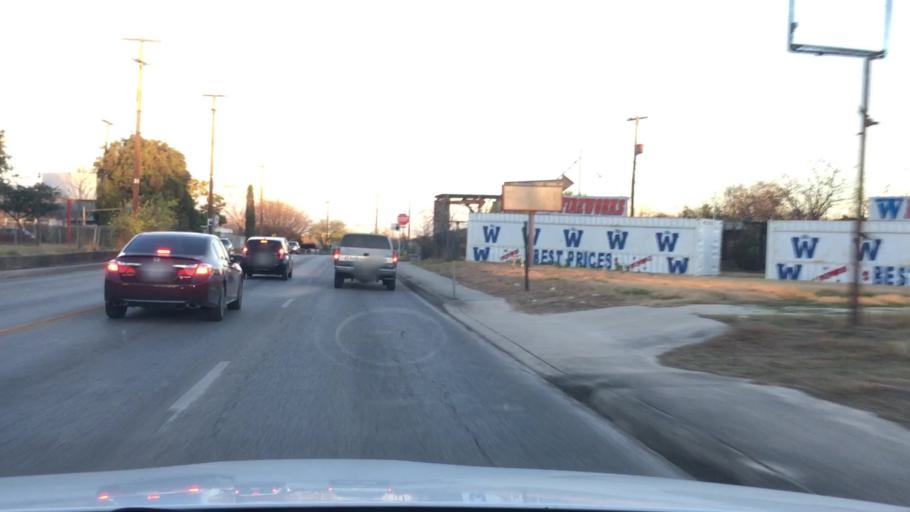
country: US
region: Texas
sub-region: Bexar County
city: Windcrest
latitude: 29.5118
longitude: -98.3622
